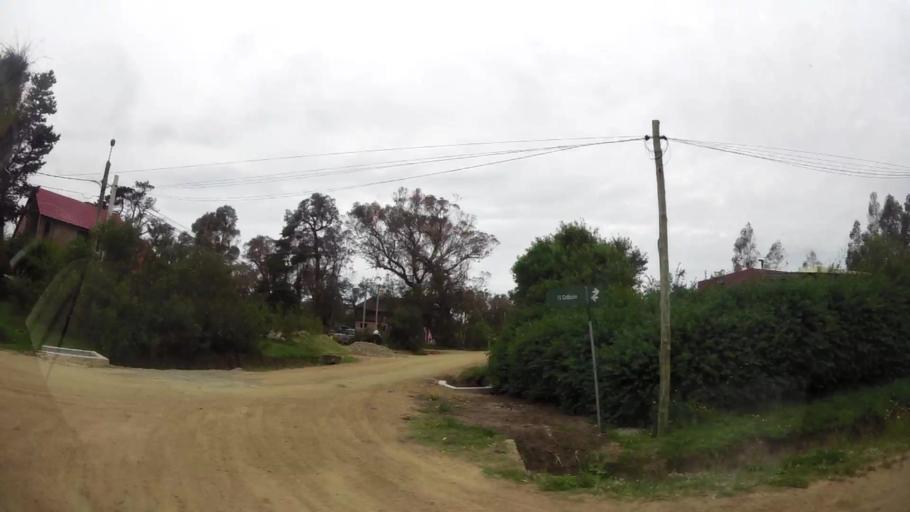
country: UY
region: Maldonado
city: Maldonado
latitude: -34.9042
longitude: -55.0369
